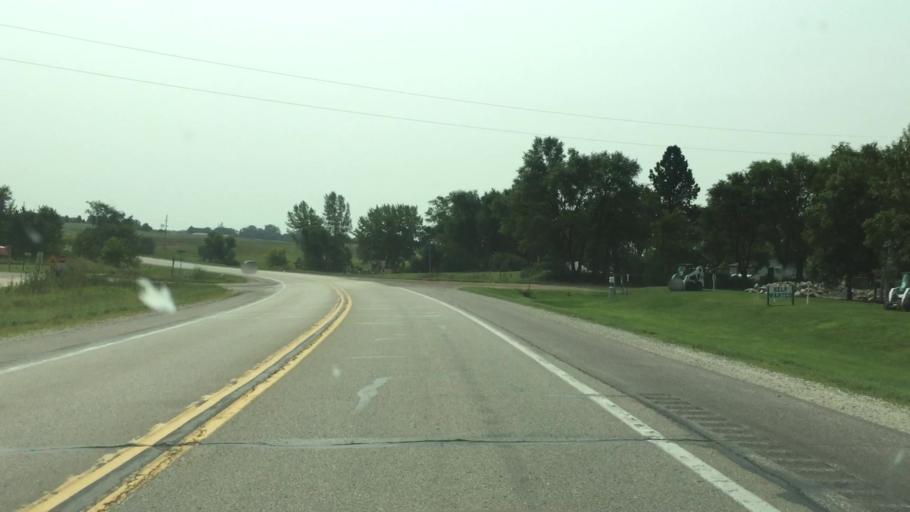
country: US
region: Iowa
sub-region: Dickinson County
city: Milford
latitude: 43.3441
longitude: -95.1783
